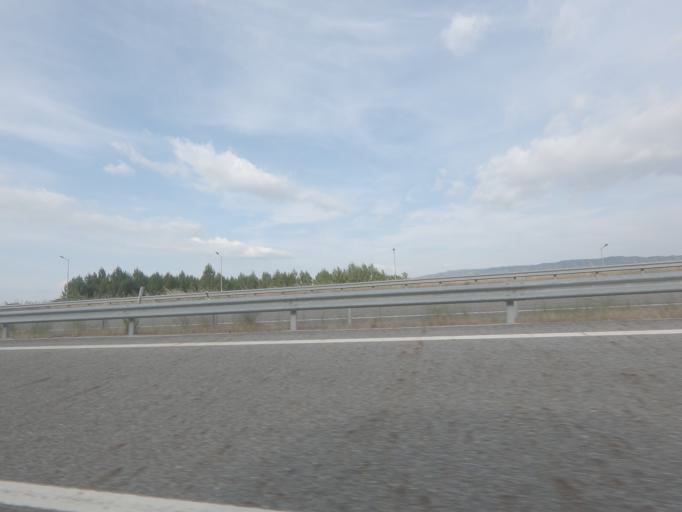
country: PT
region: Vila Real
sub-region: Chaves
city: Chaves
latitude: 41.7158
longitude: -7.5429
